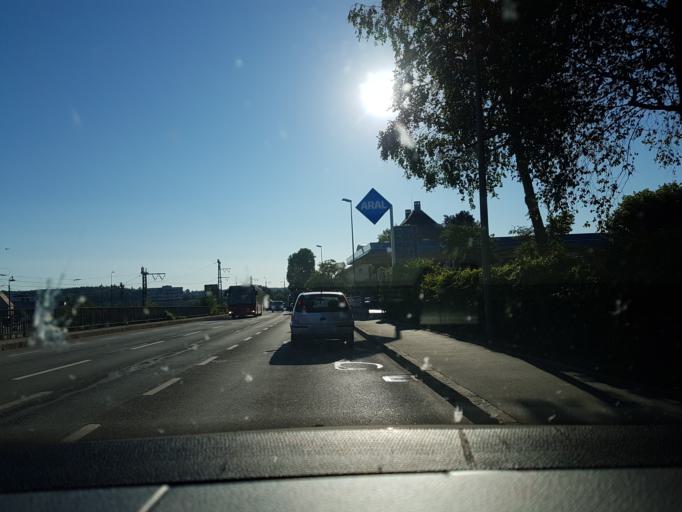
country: DE
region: Bavaria
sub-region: Upper Bavaria
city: Traunstein
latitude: 47.8669
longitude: 12.6335
